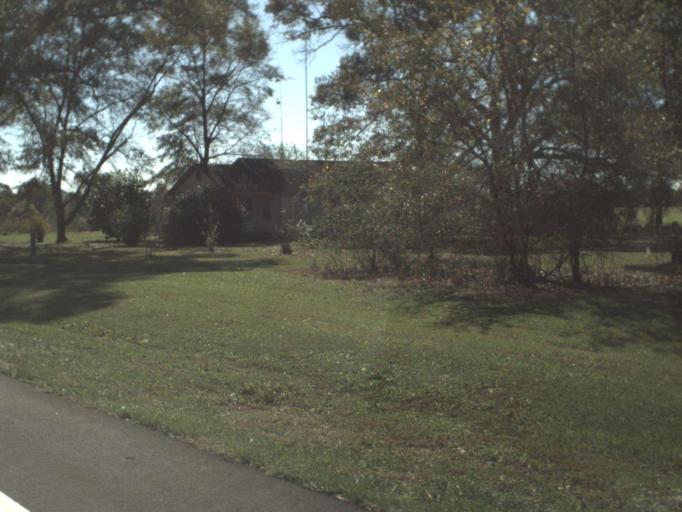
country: US
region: Alabama
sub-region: Escambia County
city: East Brewton
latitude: 30.9322
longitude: -87.0584
